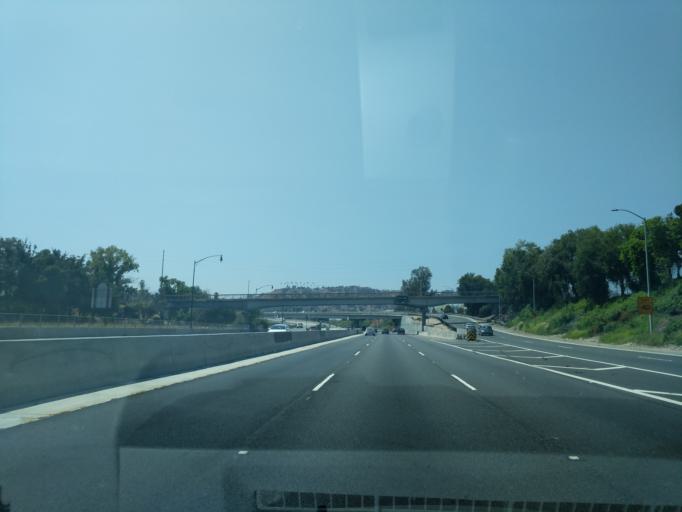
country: US
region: California
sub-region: Los Angeles County
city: Los Angeles
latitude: 34.0859
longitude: -118.2163
